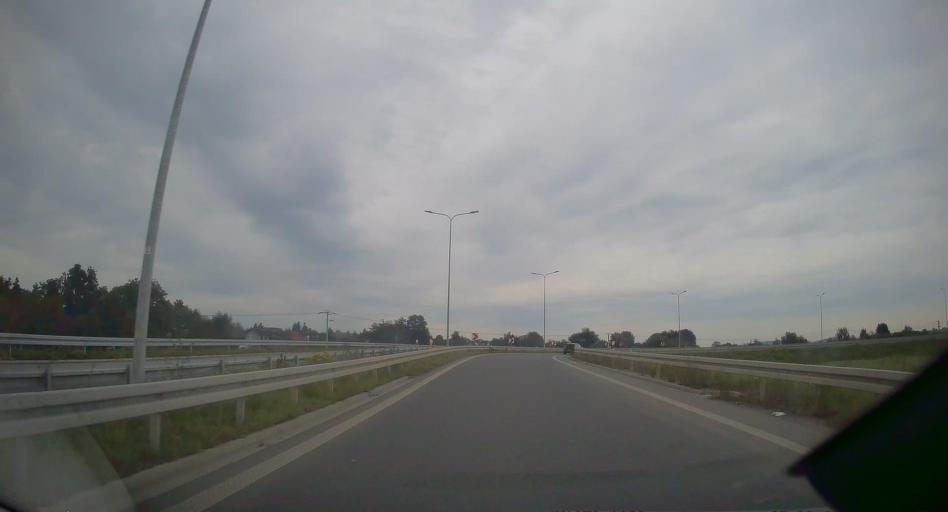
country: PL
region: Lesser Poland Voivodeship
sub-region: Powiat wielicki
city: Podleze
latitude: 50.0112
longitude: 20.1581
